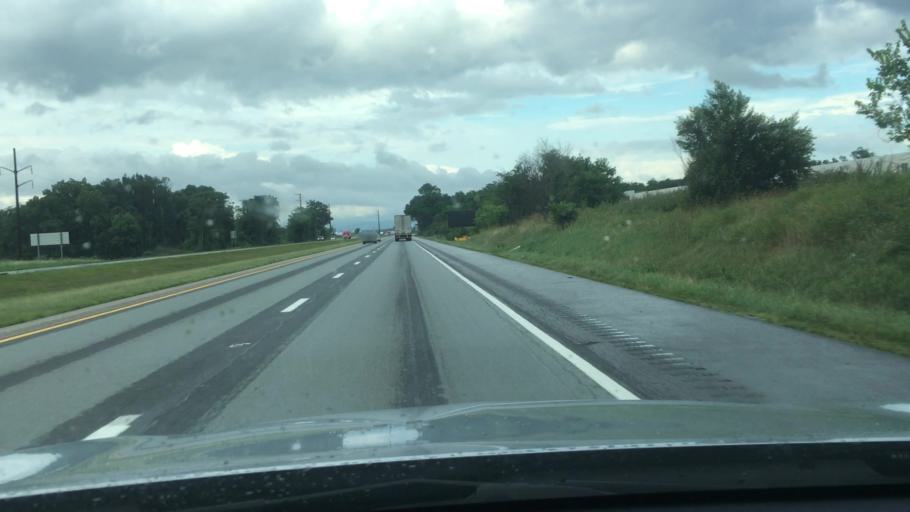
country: US
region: Pennsylvania
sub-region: Cumberland County
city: Carlisle
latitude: 40.1786
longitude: -77.2504
